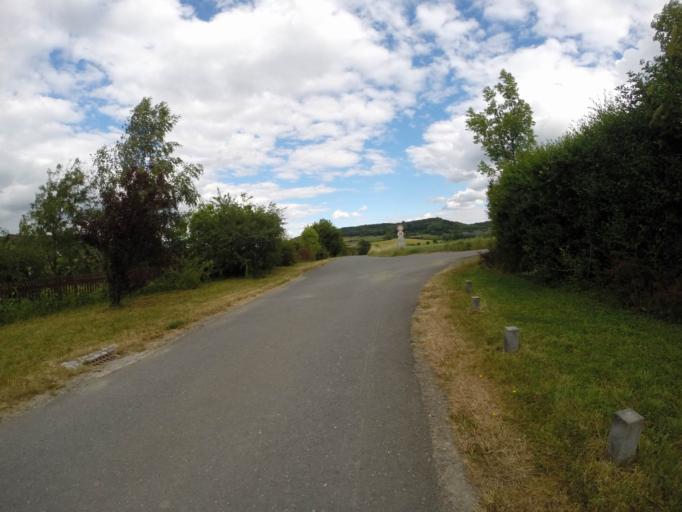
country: DE
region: Thuringia
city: Grosslobichau
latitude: 50.9269
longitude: 11.6814
